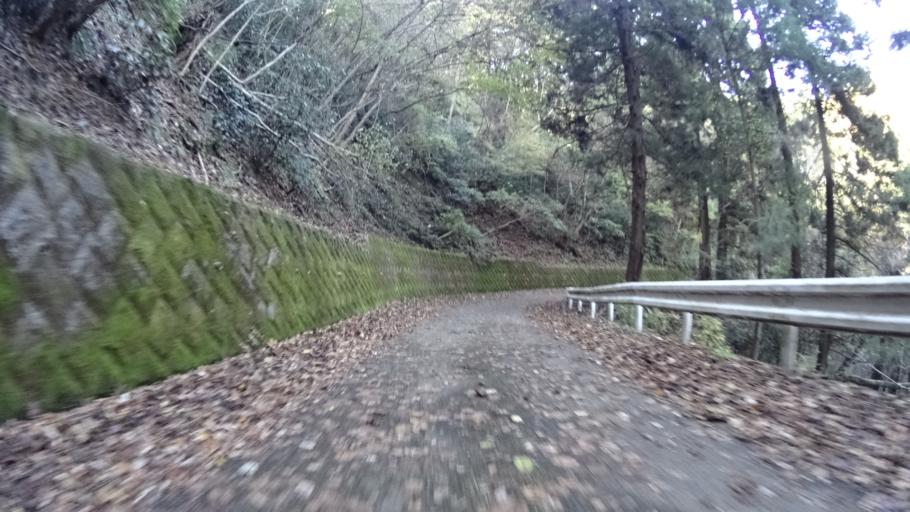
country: JP
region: Kanagawa
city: Zama
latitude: 35.5242
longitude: 139.2735
